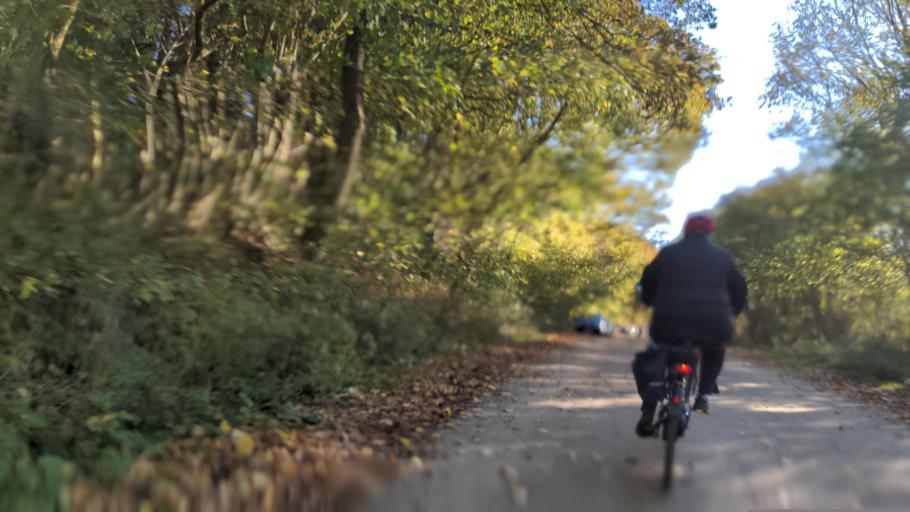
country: DE
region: Schleswig-Holstein
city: Ratekau
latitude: 53.9934
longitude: 10.6937
